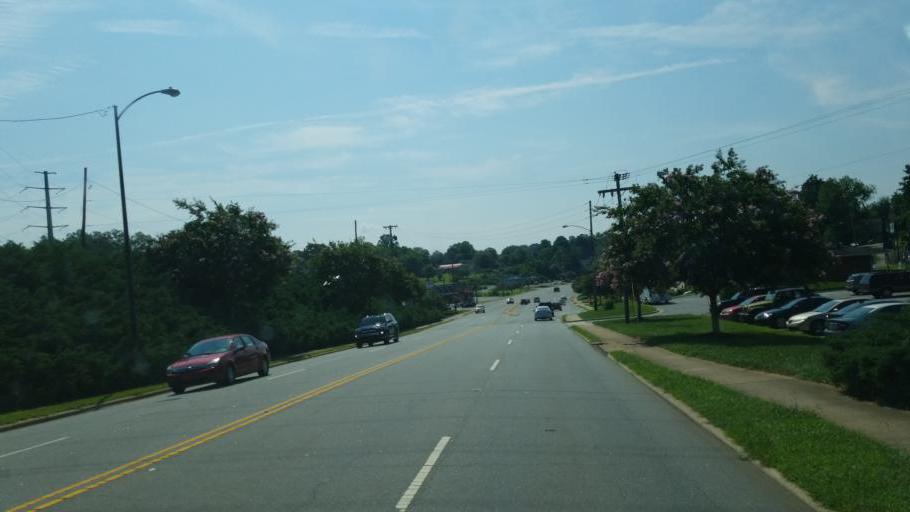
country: US
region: North Carolina
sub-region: Burke County
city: Morganton
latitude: 35.7411
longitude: -81.6821
